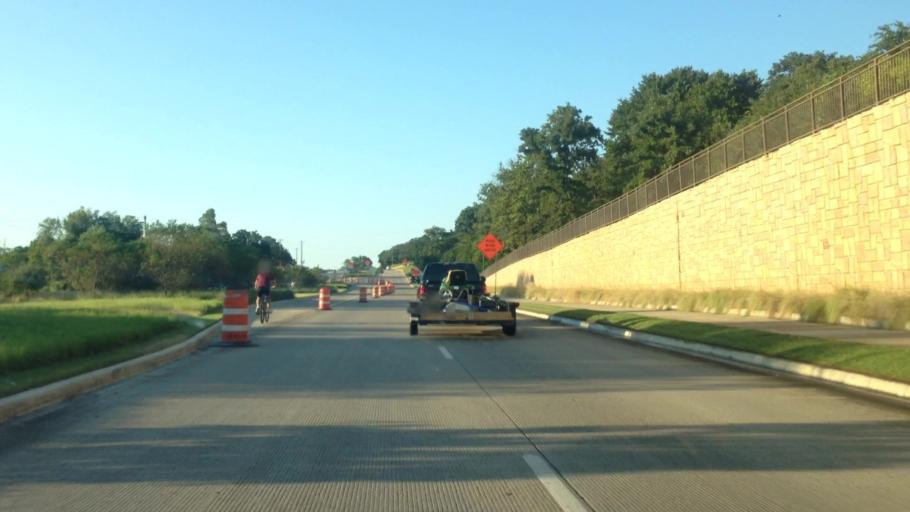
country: US
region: Texas
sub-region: Denton County
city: Trophy Club
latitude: 32.9627
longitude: -97.1860
